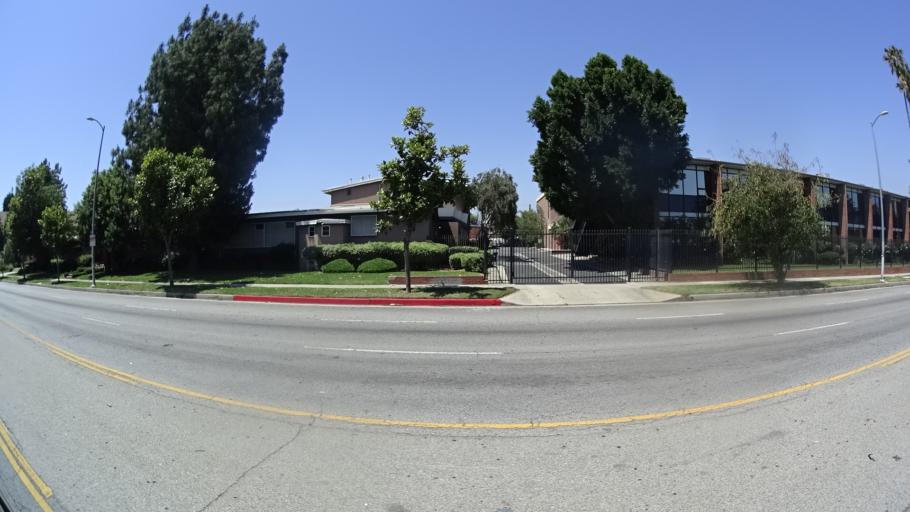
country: US
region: California
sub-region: Los Angeles County
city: Van Nuys
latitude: 34.2216
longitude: -118.4387
